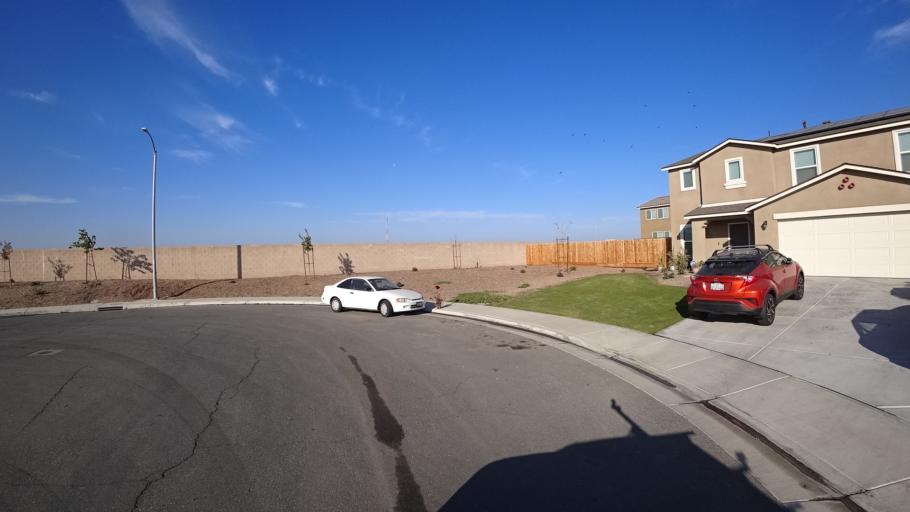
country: US
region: California
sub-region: Kern County
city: Greenfield
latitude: 35.2788
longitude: -119.0693
